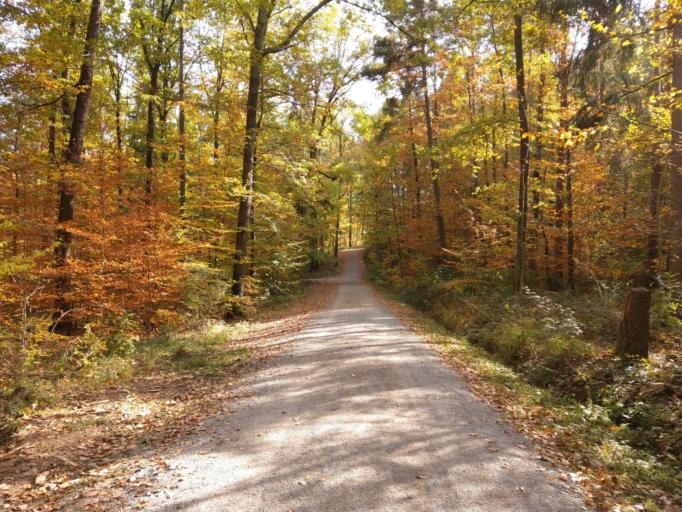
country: DE
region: Baden-Wuerttemberg
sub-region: Regierungsbezirk Stuttgart
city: Filderstadt
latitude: 48.6377
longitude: 9.2095
